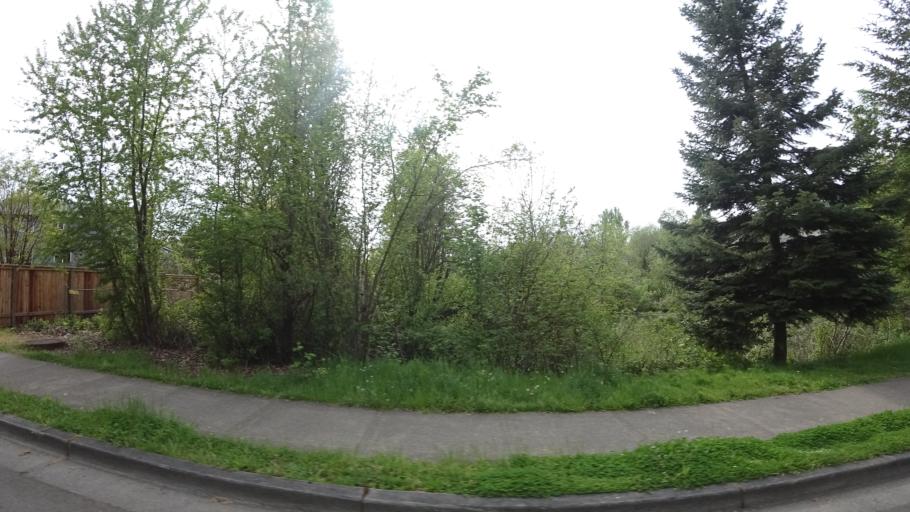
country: US
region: Oregon
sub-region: Washington County
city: Aloha
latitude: 45.5091
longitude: -122.9227
